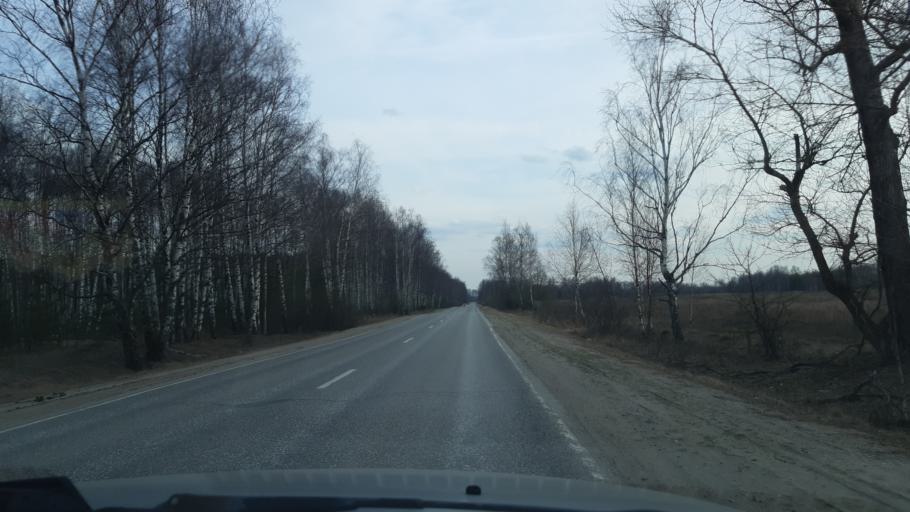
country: RU
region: Vladimir
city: Luknovo
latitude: 56.2336
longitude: 42.0343
